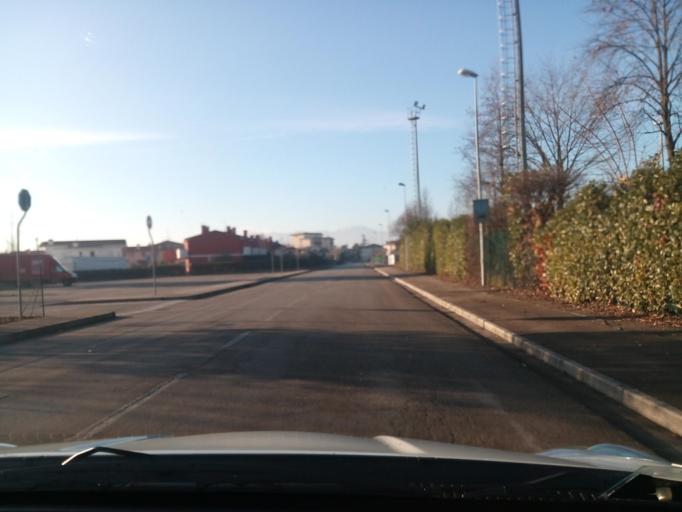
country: IT
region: Veneto
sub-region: Provincia di Vicenza
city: Dueville
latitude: 45.6328
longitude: 11.5543
